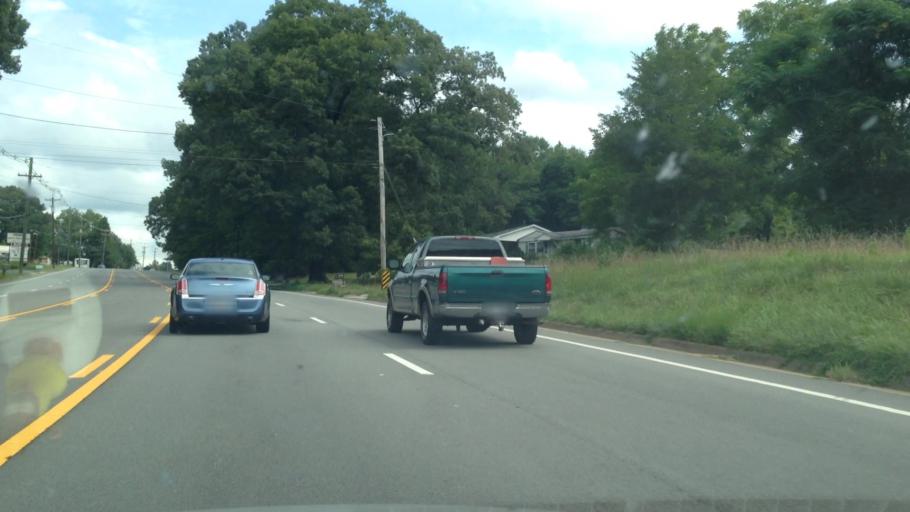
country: US
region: Virginia
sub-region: Pittsylvania County
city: Mount Hermon
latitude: 36.6550
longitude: -79.3763
